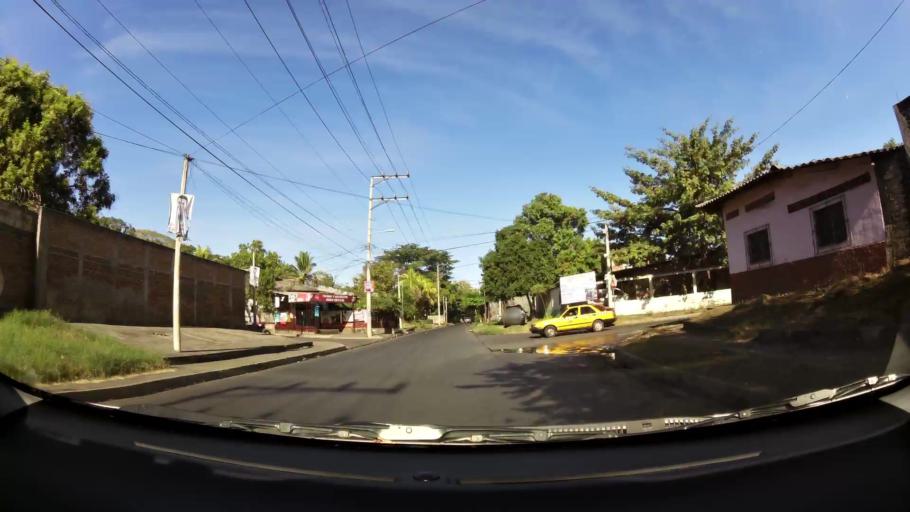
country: SV
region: San Miguel
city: San Miguel
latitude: 13.4788
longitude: -88.1898
